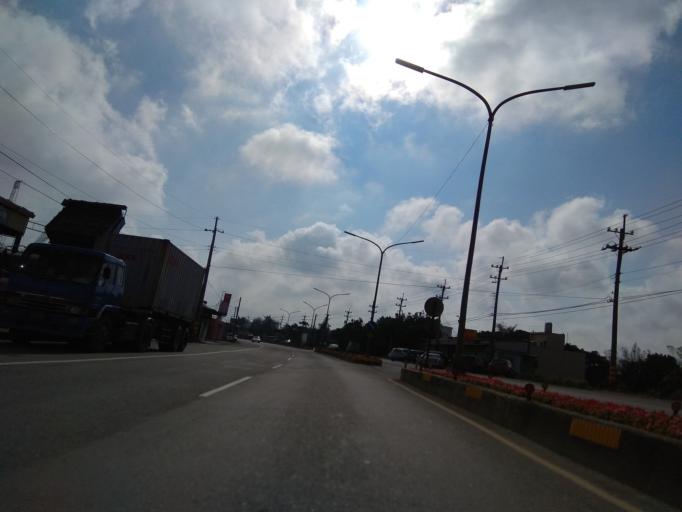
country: TW
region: Taiwan
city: Taoyuan City
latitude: 25.0407
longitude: 121.1040
